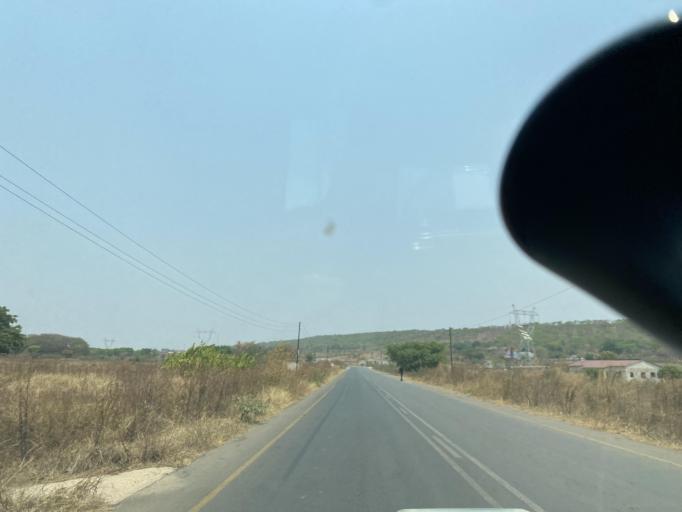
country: ZM
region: Lusaka
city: Lusaka
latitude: -15.5446
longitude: 28.4756
